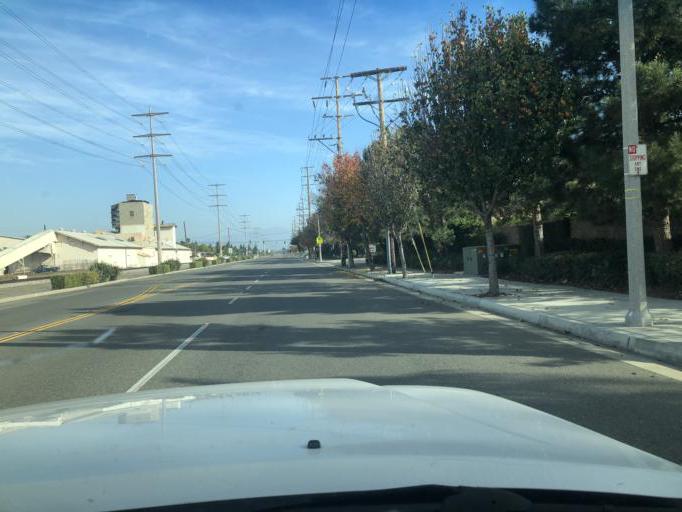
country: US
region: California
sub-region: Orange County
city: Fountain Valley
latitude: 33.7035
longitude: -117.9068
